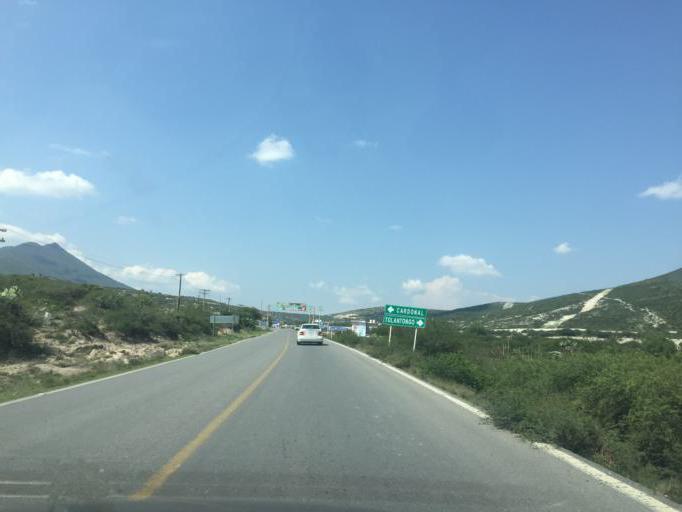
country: MX
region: Hidalgo
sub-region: Cardonal
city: Pozuelos
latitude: 20.5921
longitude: -99.1217
